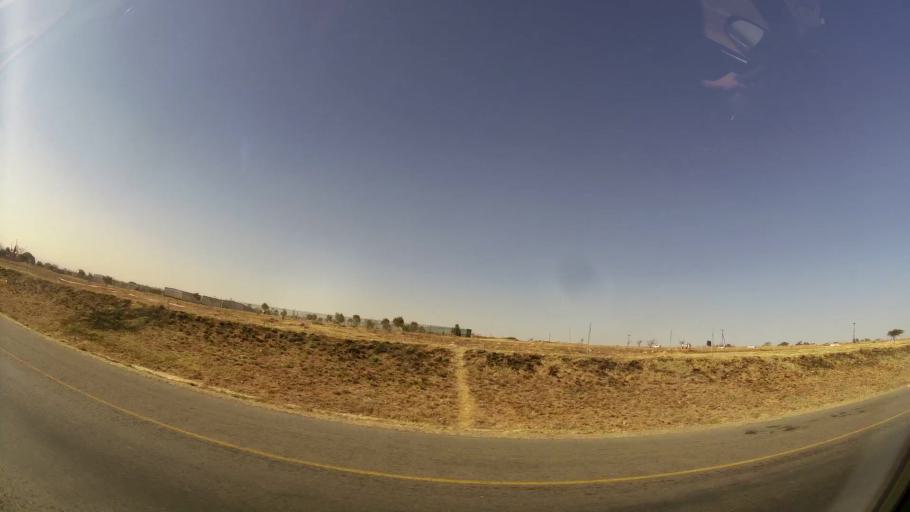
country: ZA
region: Gauteng
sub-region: West Rand District Municipality
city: Muldersdriseloop
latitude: -25.9943
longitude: 27.9253
